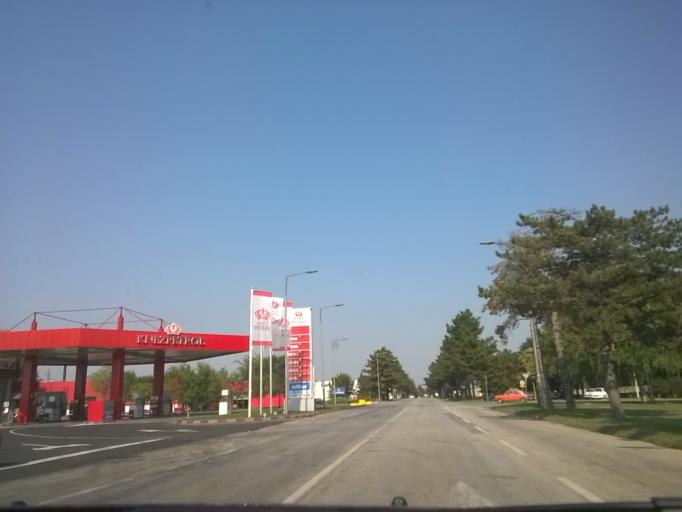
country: RS
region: Autonomna Pokrajina Vojvodina
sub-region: Juznobanatski Okrug
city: Vrsac
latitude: 45.1022
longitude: 21.2747
